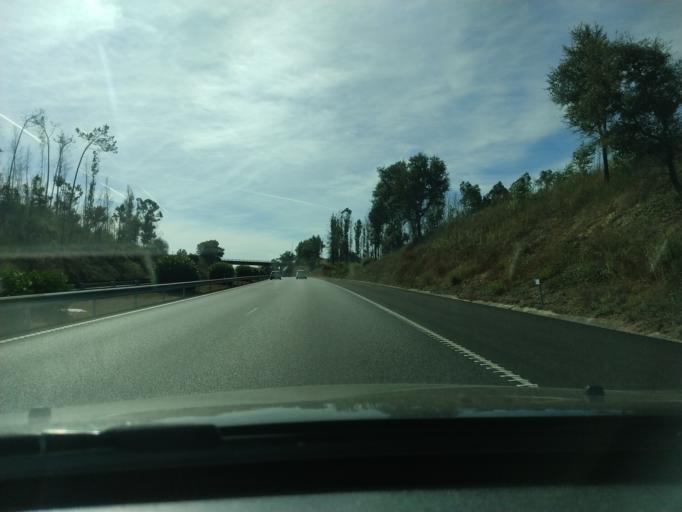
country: PT
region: Aveiro
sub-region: Mealhada
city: Pampilhosa do Botao
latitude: 40.3119
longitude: -8.4895
